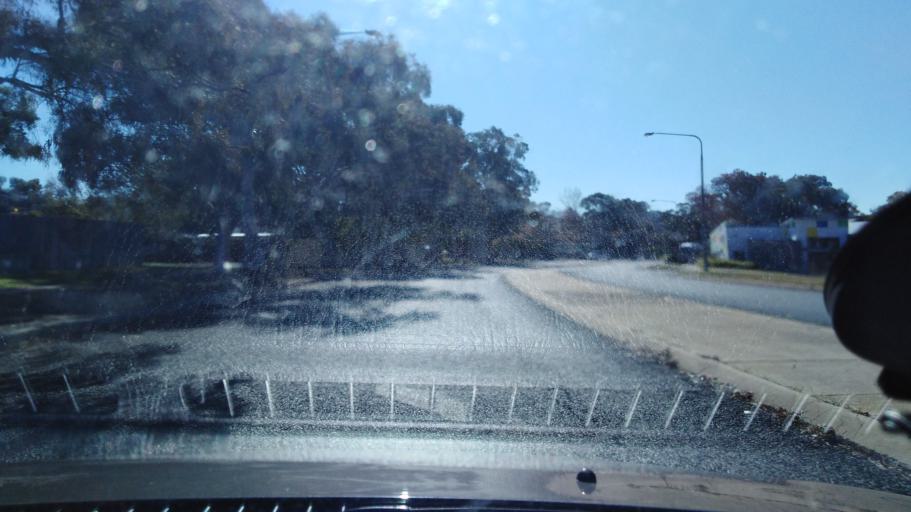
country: AU
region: Australian Capital Territory
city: Forrest
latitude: -35.3482
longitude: 149.0359
